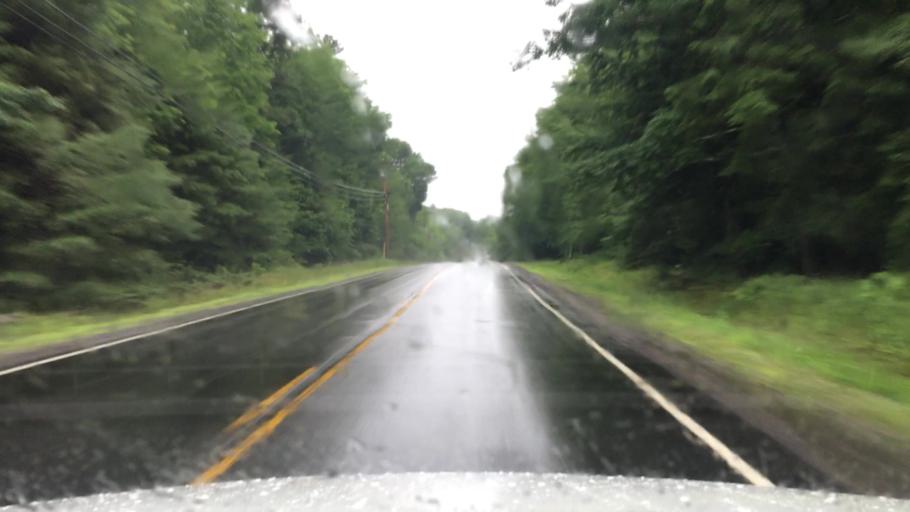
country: US
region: Maine
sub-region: Kennebec County
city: Manchester
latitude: 44.3151
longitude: -69.8413
